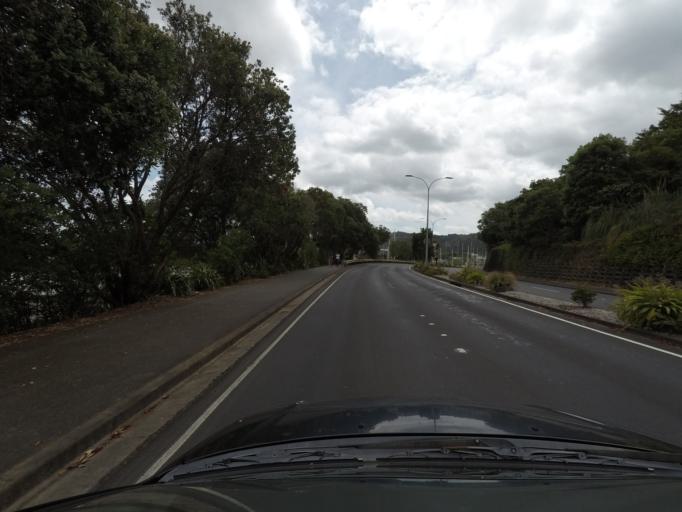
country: NZ
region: Northland
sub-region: Whangarei
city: Whangarei
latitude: -35.7247
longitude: 174.3290
